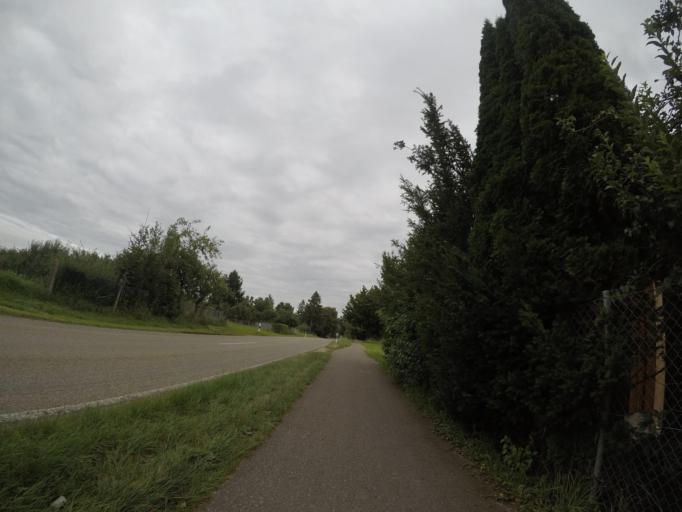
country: DE
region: Baden-Wuerttemberg
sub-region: Tuebingen Region
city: Langenau
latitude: 48.4866
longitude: 10.1055
